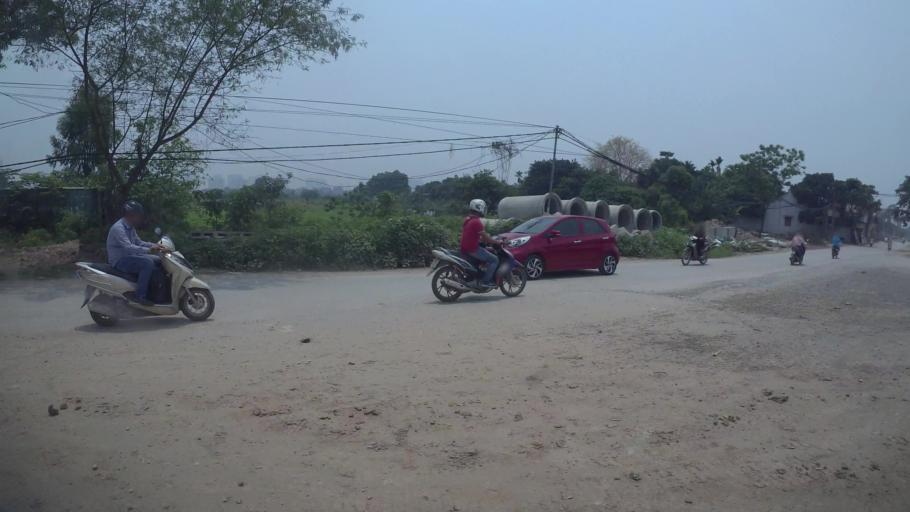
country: VN
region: Ha Noi
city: Ha Dong
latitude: 21.0022
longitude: 105.7666
